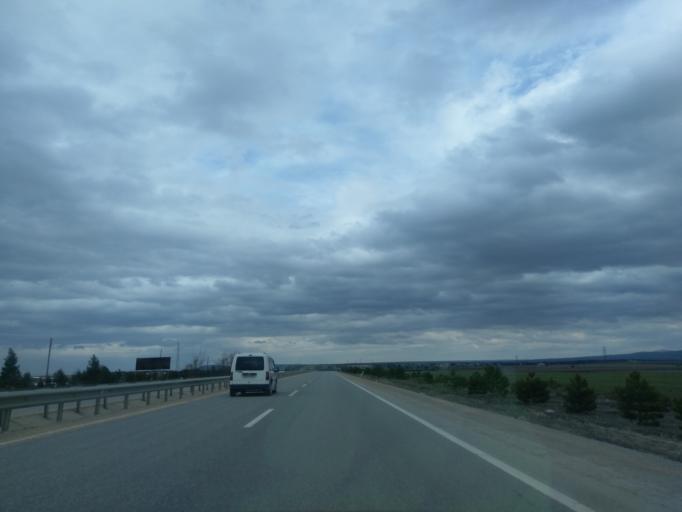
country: TR
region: Eskisehir
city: Inonu
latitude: 39.7256
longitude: 30.3165
